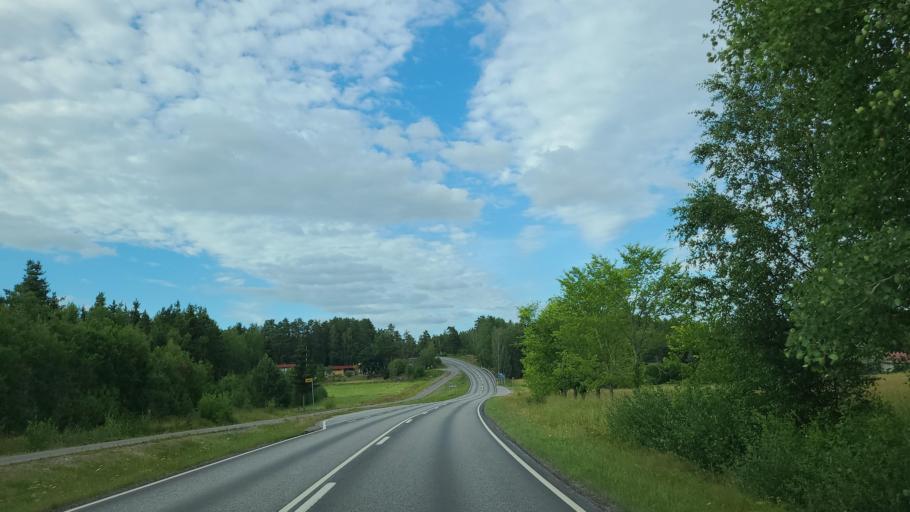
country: FI
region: Varsinais-Suomi
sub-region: Turku
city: Rymaettylae
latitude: 60.4085
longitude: 21.8954
